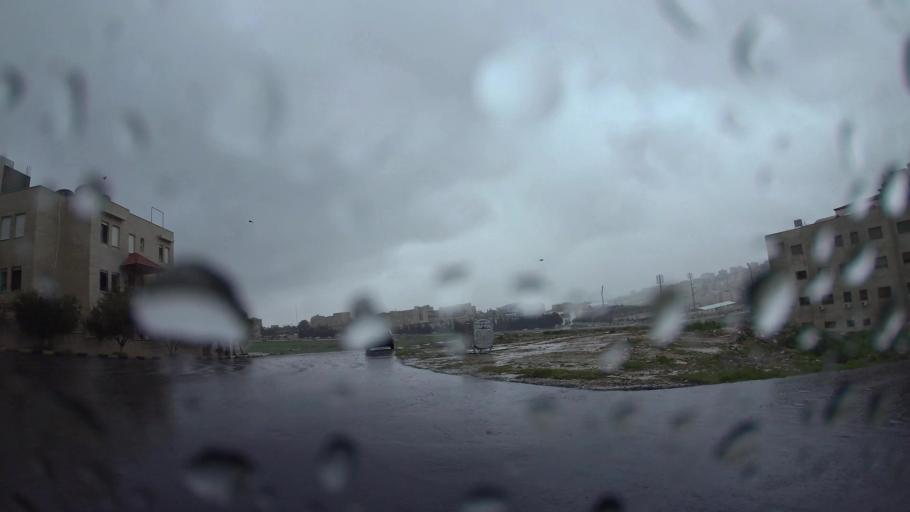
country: JO
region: Amman
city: Al Jubayhah
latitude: 32.0421
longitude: 35.8939
